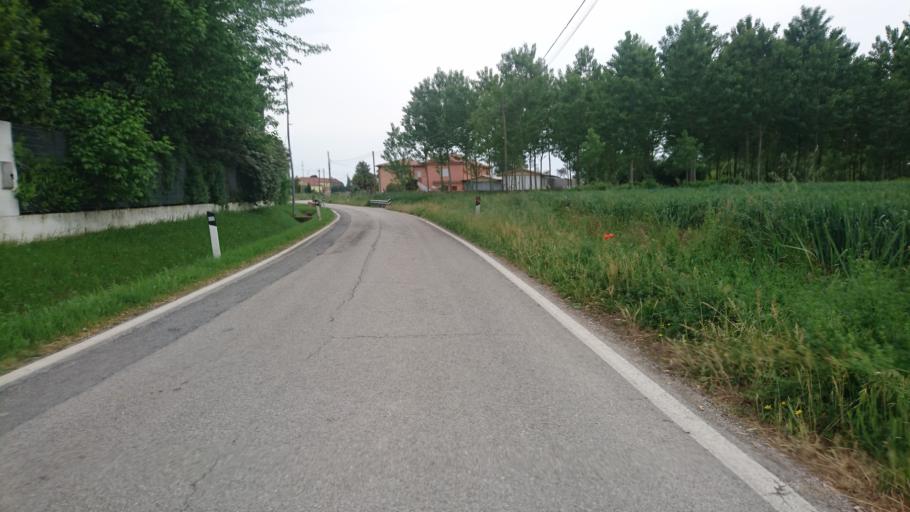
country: IT
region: Veneto
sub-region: Provincia di Padova
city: Sant'Elena
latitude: 45.1730
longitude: 11.7227
